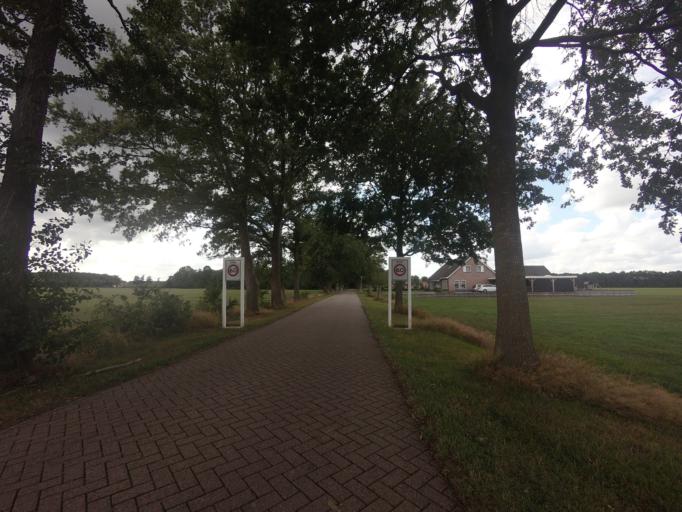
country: NL
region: Drenthe
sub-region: Gemeente Westerveld
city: Dwingeloo
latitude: 52.9642
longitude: 6.2863
